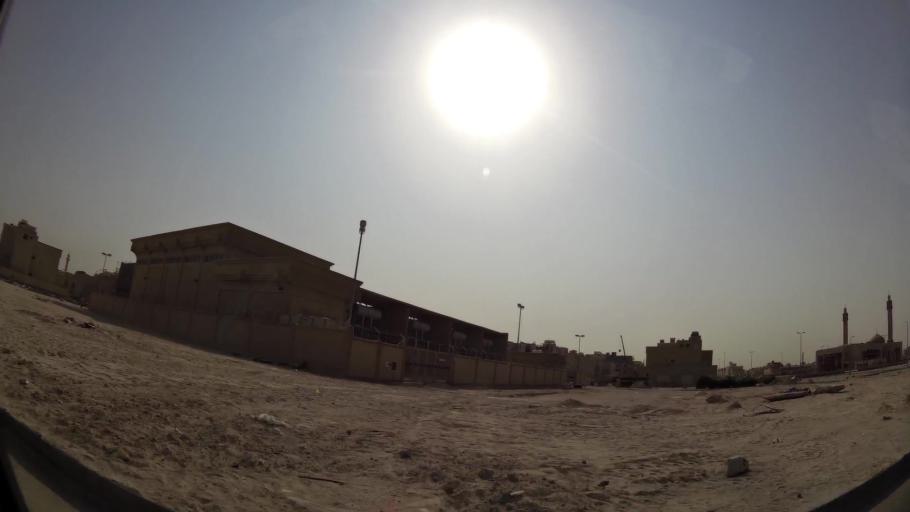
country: KW
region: Muhafazat al Jahra'
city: Al Jahra'
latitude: 29.3544
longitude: 47.7573
